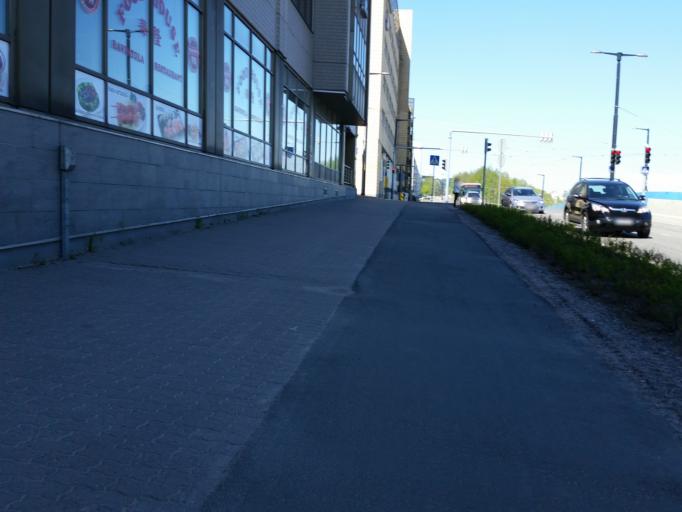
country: FI
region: Uusimaa
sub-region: Helsinki
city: Helsinki
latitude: 60.1969
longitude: 24.9285
